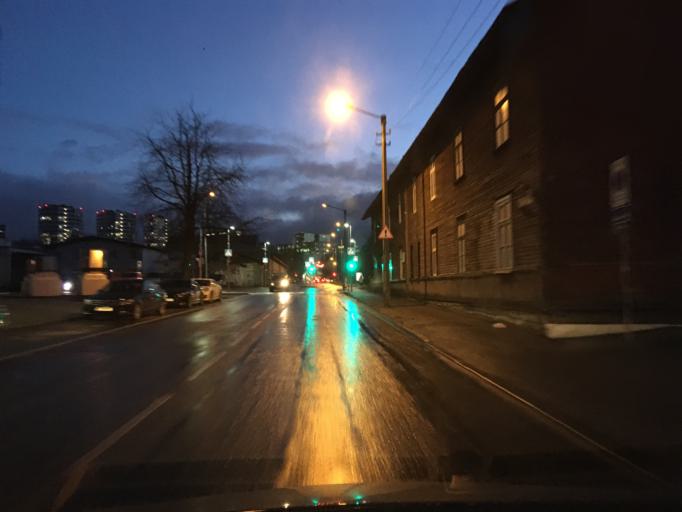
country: EE
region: Harju
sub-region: Tallinna linn
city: Tallinn
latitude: 59.4324
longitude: 24.7787
